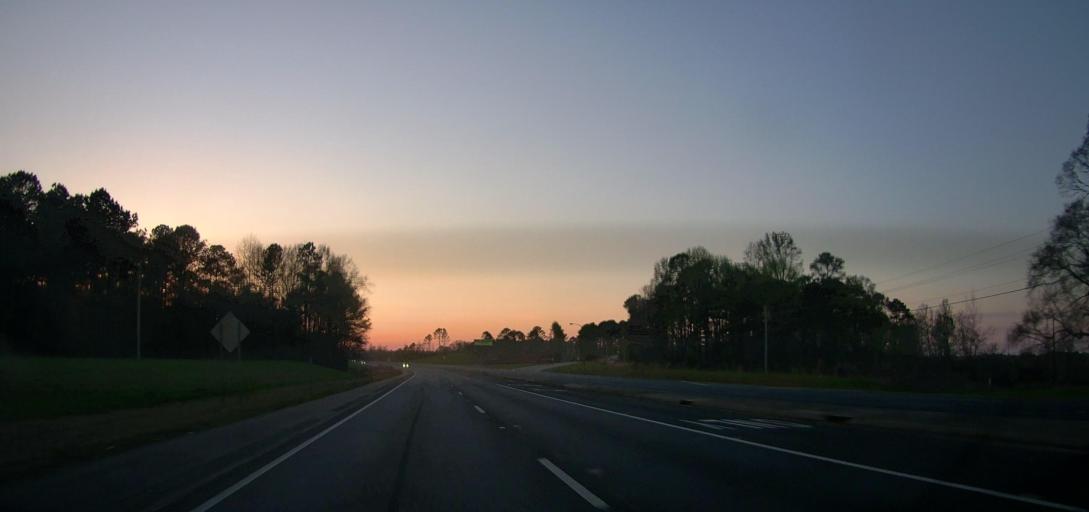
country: US
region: Alabama
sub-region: Tallapoosa County
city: Alexander City
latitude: 32.9049
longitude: -85.8982
